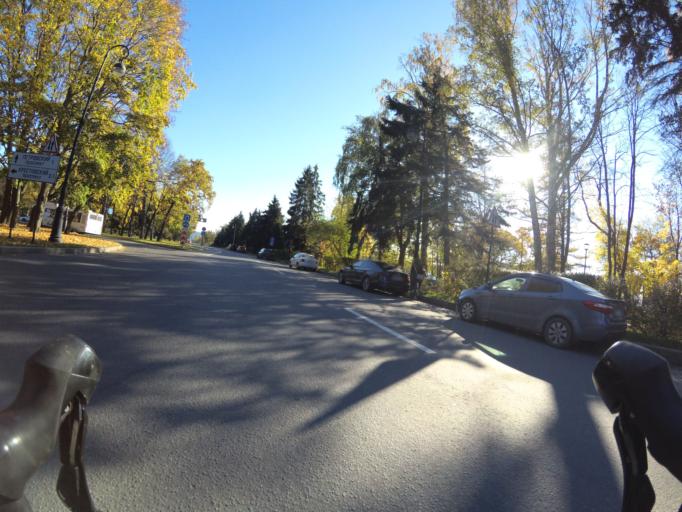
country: RU
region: Leningrad
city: Krestovskiy ostrov
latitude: 59.9677
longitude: 30.2477
